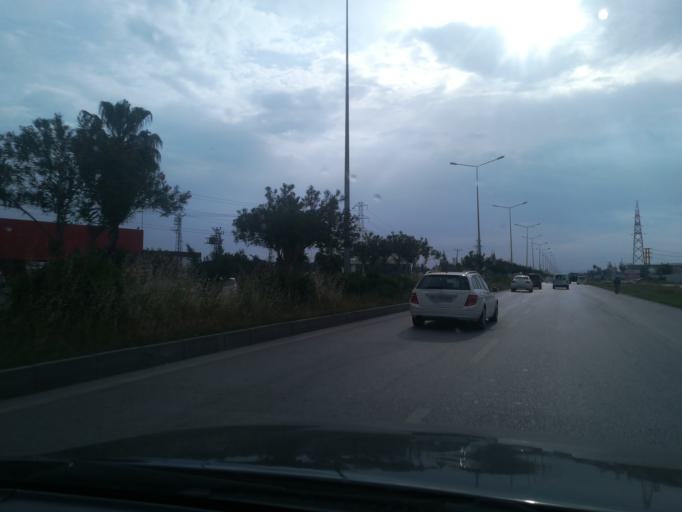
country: TR
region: Adana
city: Yuregir
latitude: 36.9828
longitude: 35.4072
